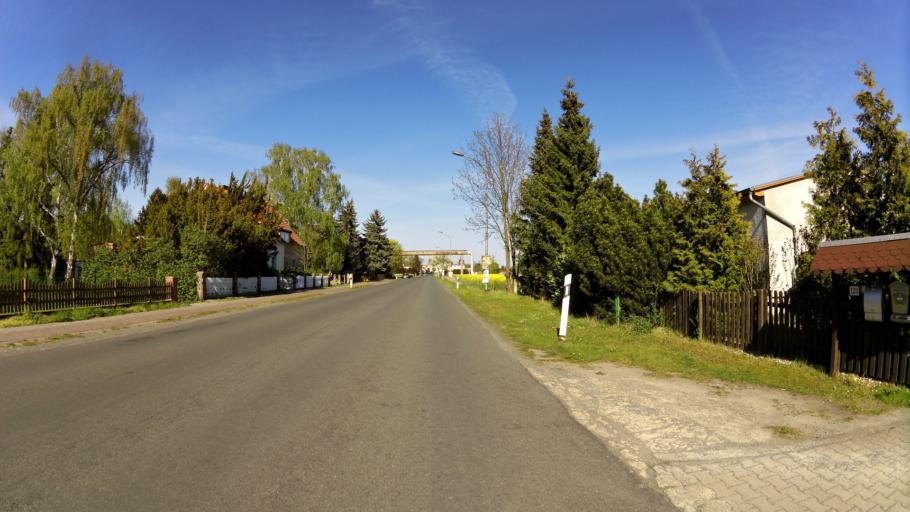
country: DE
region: Saxony-Anhalt
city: Stendal
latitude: 52.5866
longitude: 11.8330
